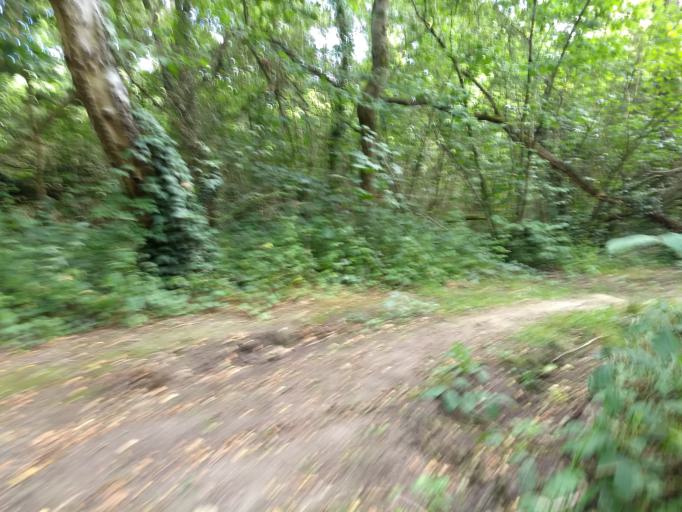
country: GB
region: England
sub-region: Isle of Wight
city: Newport
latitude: 50.7185
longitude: -1.2595
